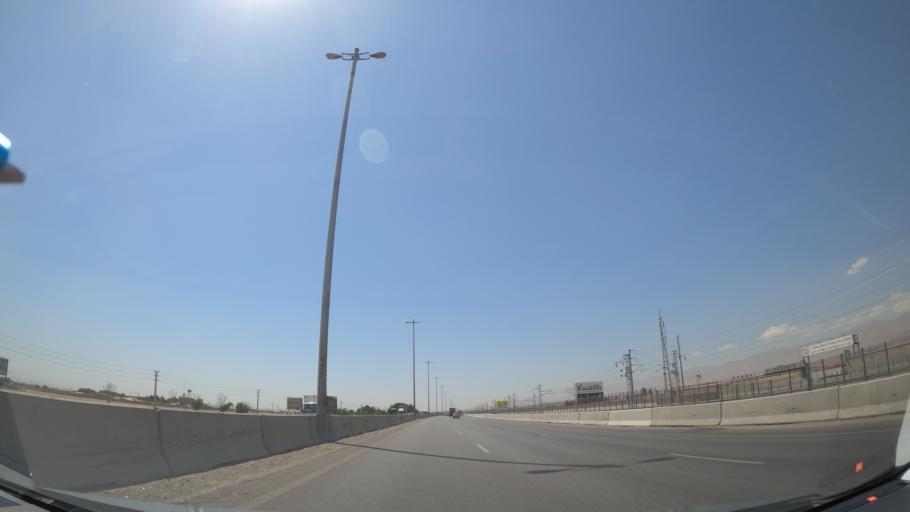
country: IR
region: Alborz
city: Hashtgerd
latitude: 35.9189
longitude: 50.7864
